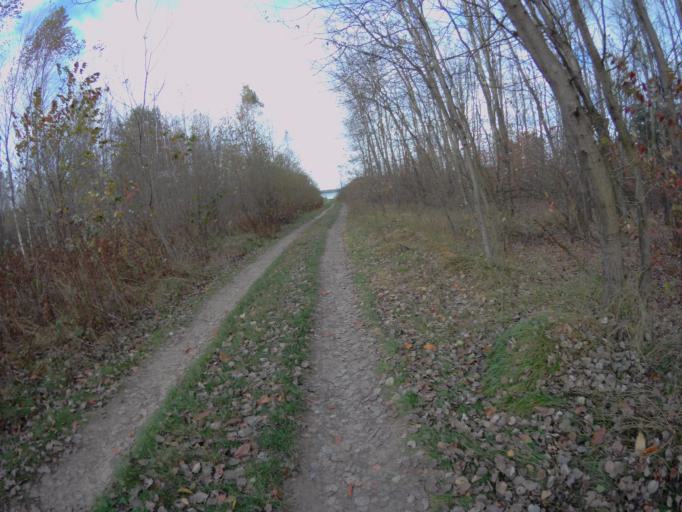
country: PL
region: Subcarpathian Voivodeship
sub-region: Powiat kolbuszowski
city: Lipnica
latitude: 50.3244
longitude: 21.9414
